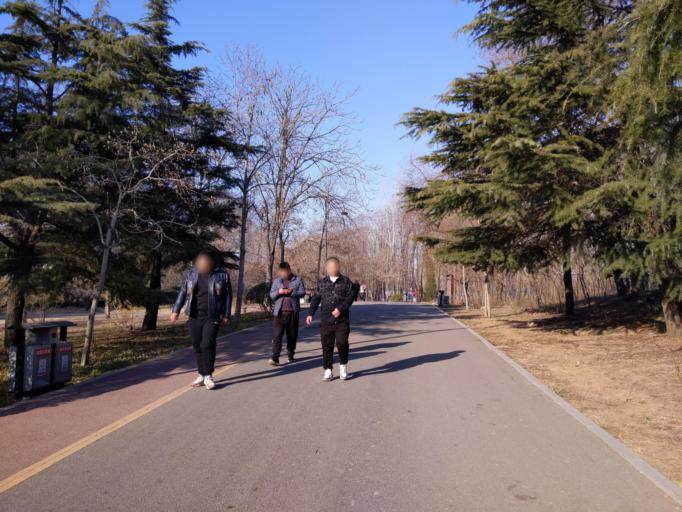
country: CN
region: Henan Sheng
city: Puyang
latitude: 35.7761
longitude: 114.9638
